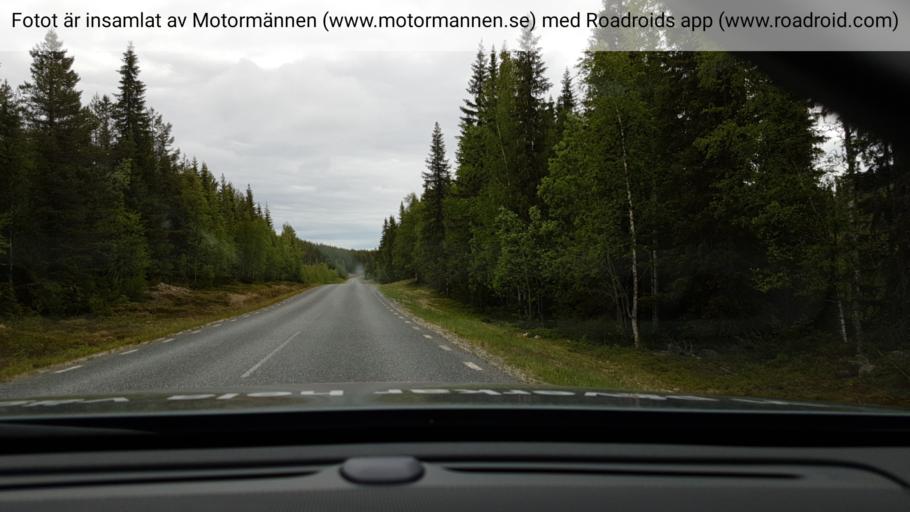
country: SE
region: Vaesterbotten
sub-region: Asele Kommun
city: Insjon
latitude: 64.3501
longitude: 17.8260
